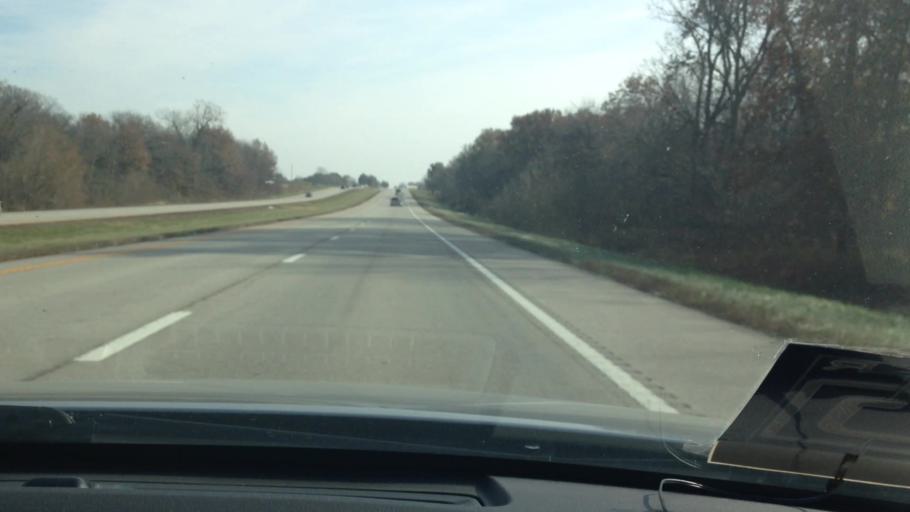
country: US
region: Missouri
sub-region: Cass County
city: Garden City
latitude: 38.6028
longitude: -94.2719
